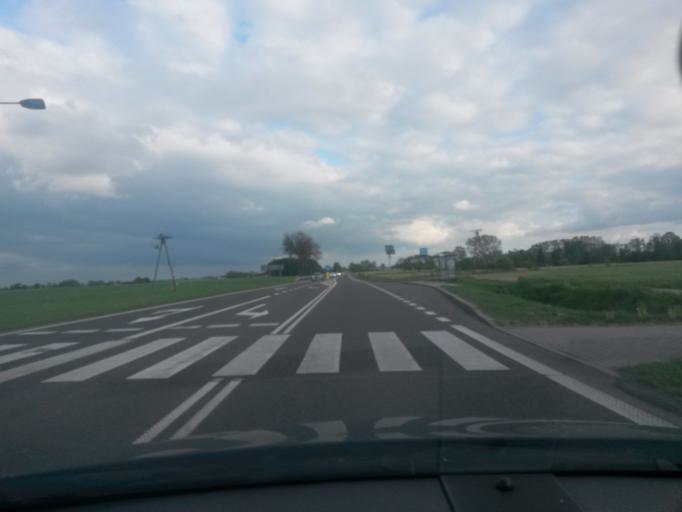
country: PL
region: Masovian Voivodeship
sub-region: Powiat plocki
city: Drobin
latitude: 52.7026
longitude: 20.0371
